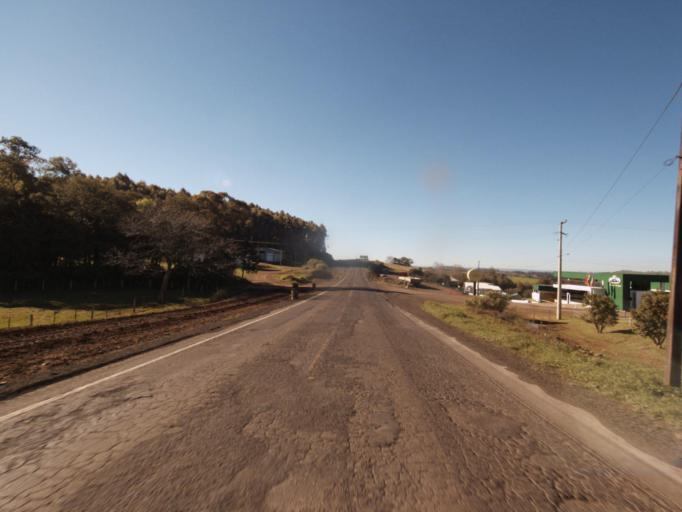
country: AR
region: Misiones
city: Bernardo de Irigoyen
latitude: -26.6302
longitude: -53.5174
